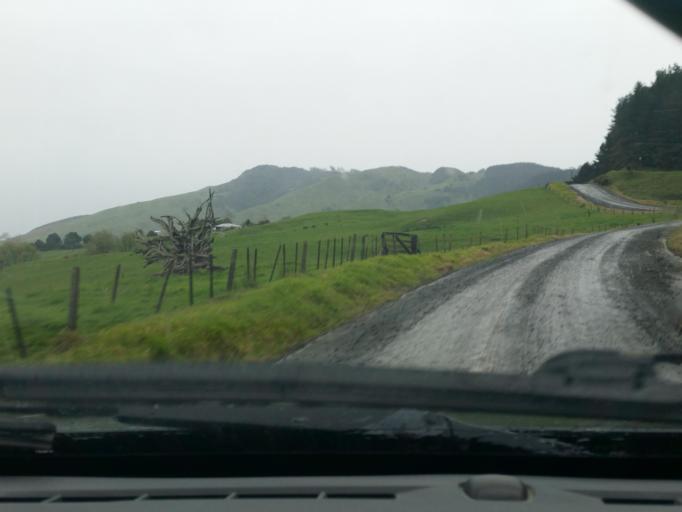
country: NZ
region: Northland
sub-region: Kaipara District
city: Dargaville
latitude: -35.8177
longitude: 173.8111
